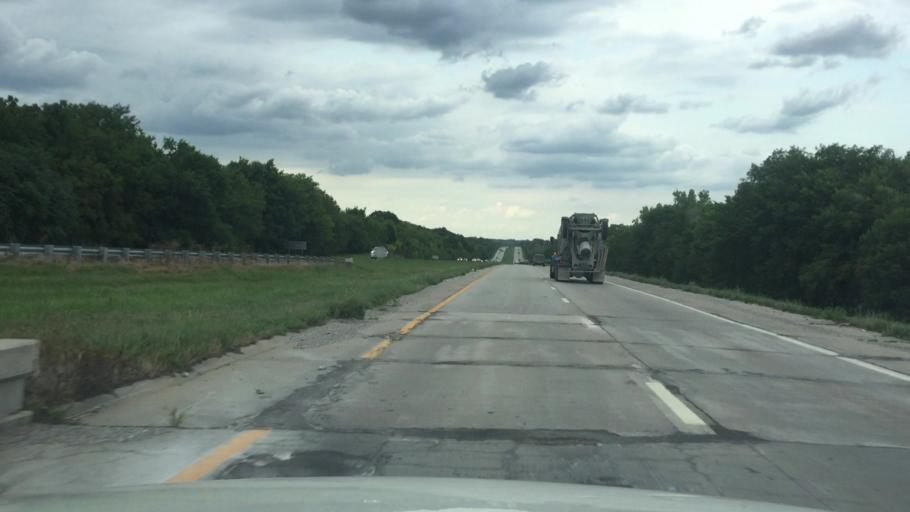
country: US
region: Missouri
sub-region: Cass County
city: Belton
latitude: 38.7820
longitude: -94.6775
